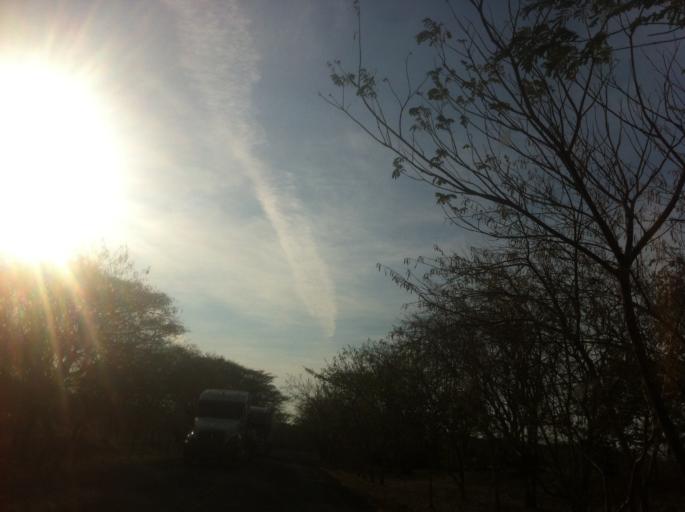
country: NI
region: Rivas
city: Cardenas
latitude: 11.2818
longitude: -85.6717
